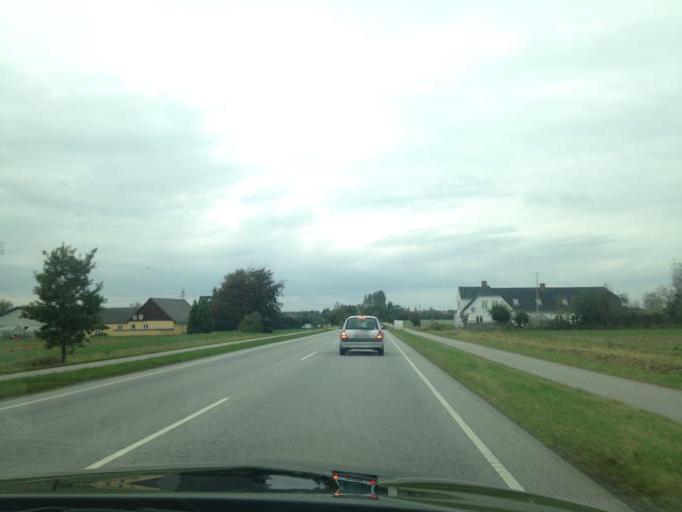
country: DK
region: South Denmark
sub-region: Kolding Kommune
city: Christiansfeld
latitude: 55.3391
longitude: 9.4887
